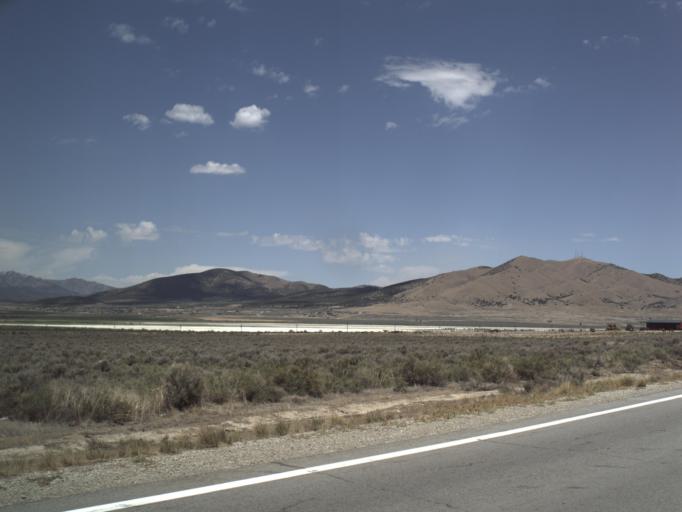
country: US
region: Utah
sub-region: Tooele County
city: Tooele
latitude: 40.4007
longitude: -112.3859
